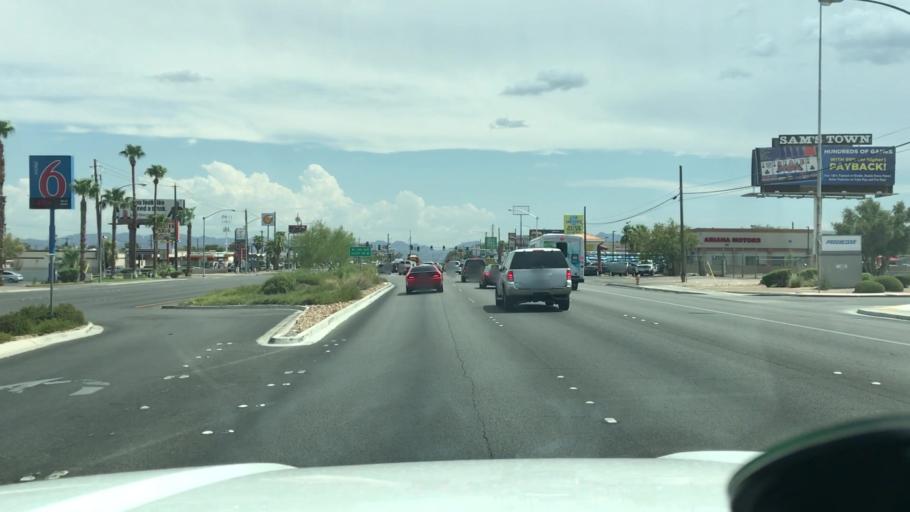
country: US
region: Nevada
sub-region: Clark County
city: Winchester
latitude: 36.1316
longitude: -115.0857
